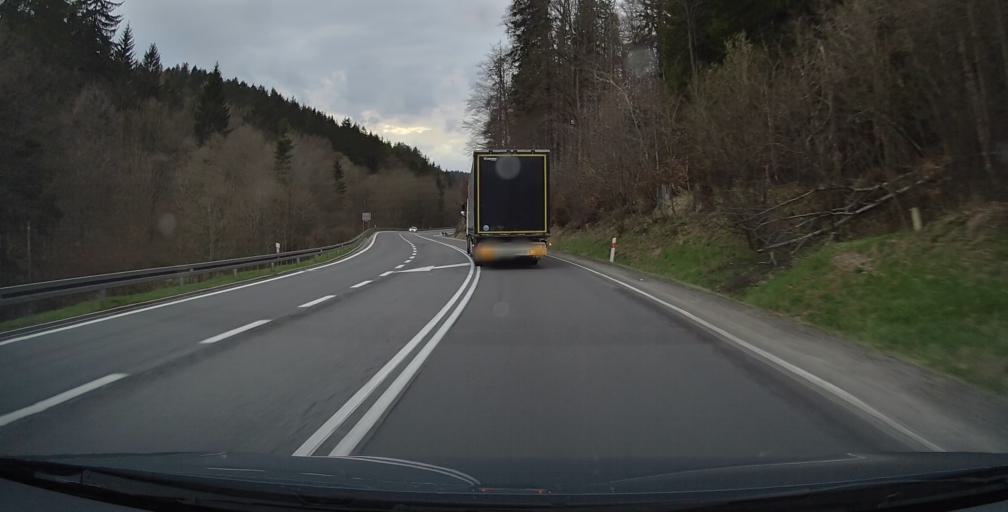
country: PL
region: Lower Silesian Voivodeship
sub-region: Powiat klodzki
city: Lewin Klodzki
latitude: 50.4063
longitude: 16.3319
